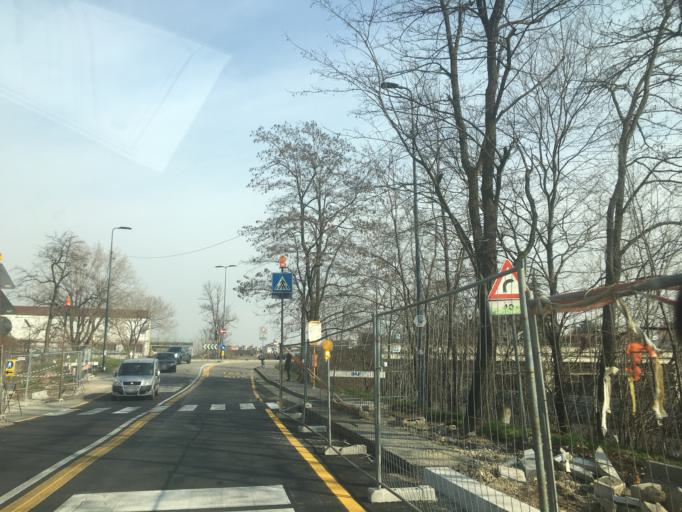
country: IT
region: Lombardy
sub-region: Citta metropolitana di Milano
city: Sesto San Giovanni
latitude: 45.5227
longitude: 9.2216
